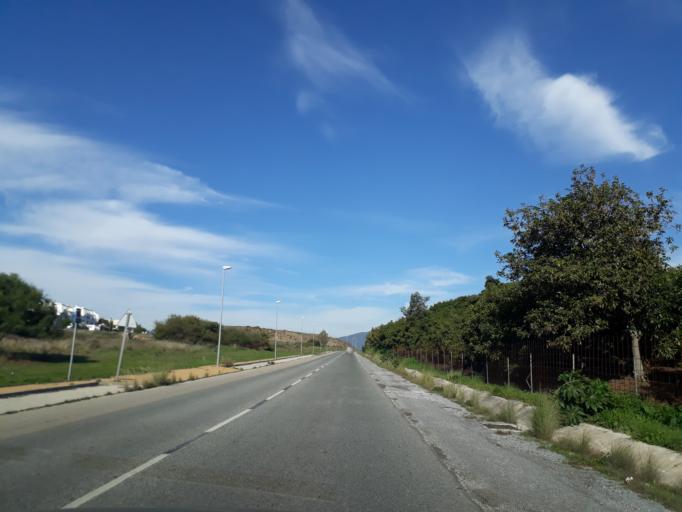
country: ES
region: Andalusia
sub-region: Provincia de Malaga
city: Fuengirola
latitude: 36.5276
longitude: -4.6859
